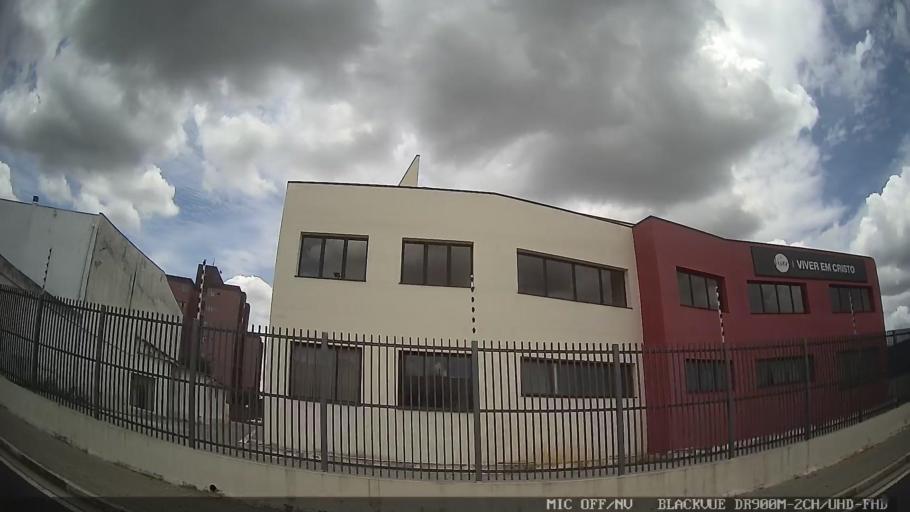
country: BR
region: Sao Paulo
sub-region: Suzano
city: Suzano
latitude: -23.5476
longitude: -46.3040
